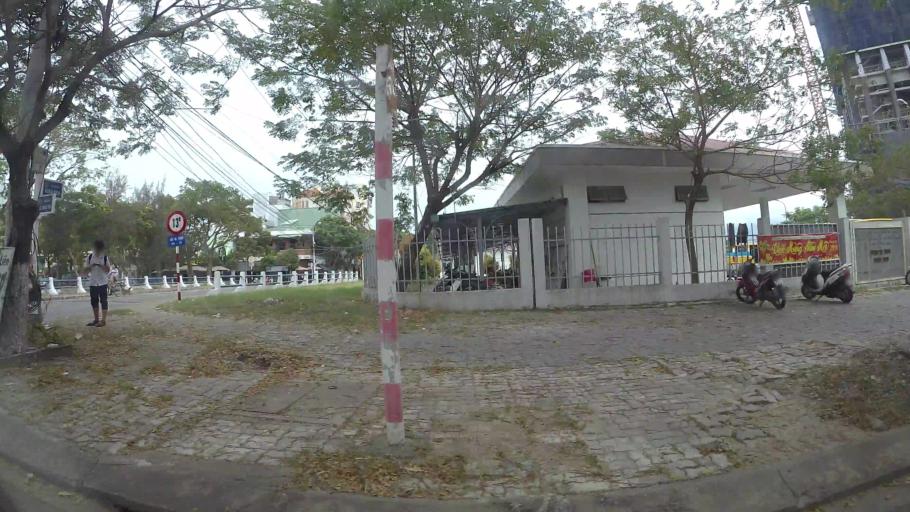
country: VN
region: Da Nang
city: Da Nang
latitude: 16.0868
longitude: 108.2204
